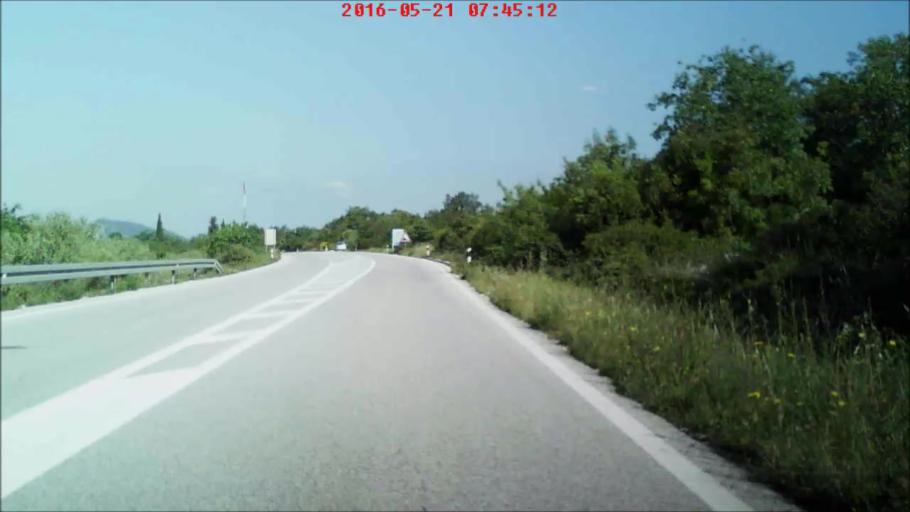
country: HR
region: Dubrovacko-Neretvanska
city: Podgora
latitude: 42.8215
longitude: 17.7683
